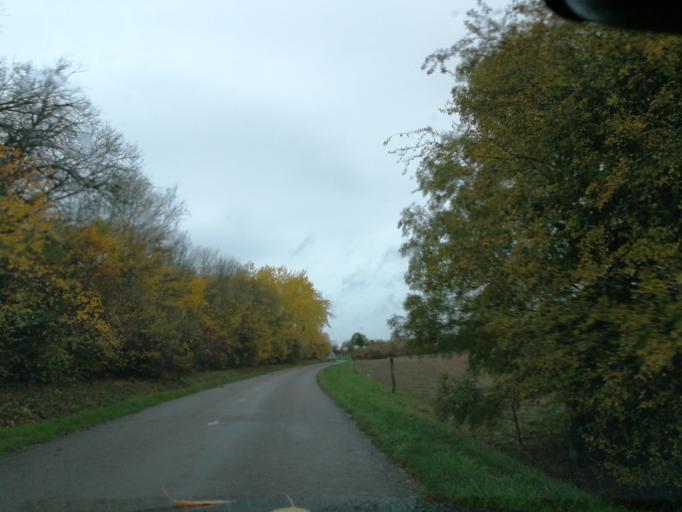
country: FR
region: Bourgogne
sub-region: Departement de la Cote-d'Or
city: Fleurey-sur-Ouche
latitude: 47.3285
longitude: 4.7892
